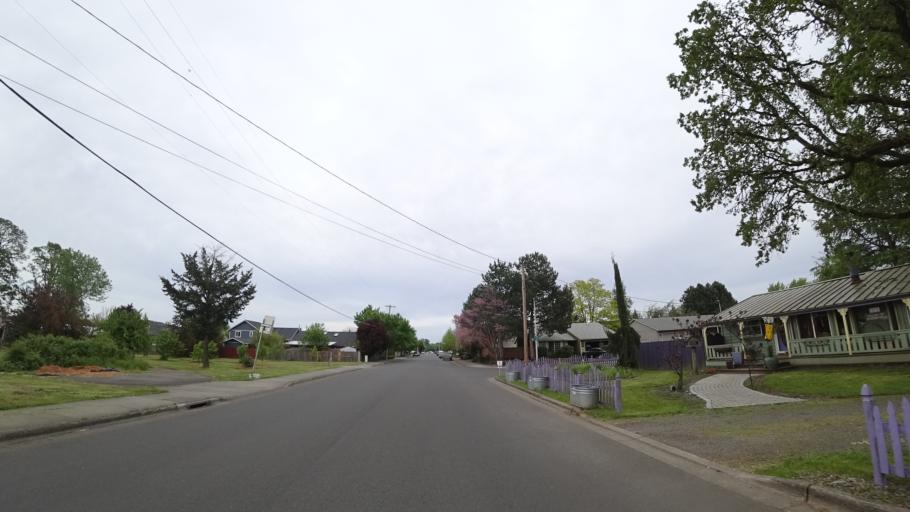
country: US
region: Oregon
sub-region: Washington County
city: Aloha
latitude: 45.5122
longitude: -122.9094
